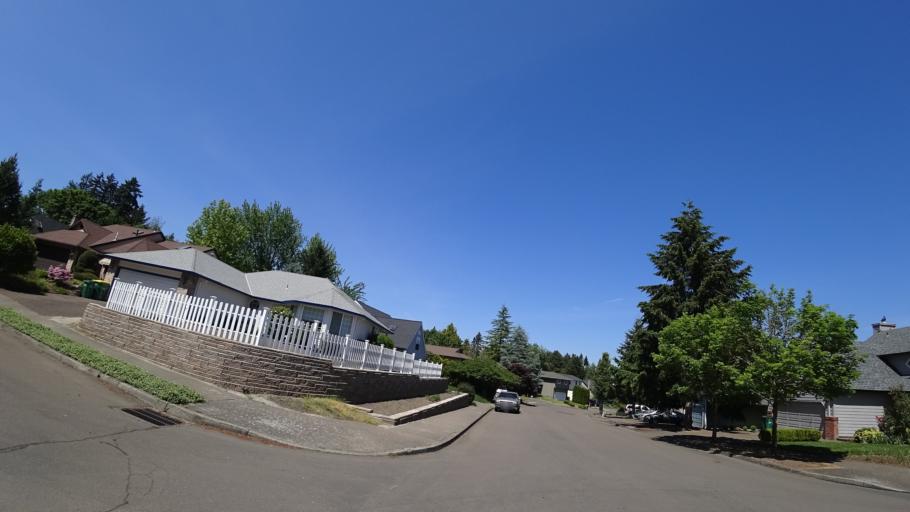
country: US
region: Oregon
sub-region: Washington County
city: King City
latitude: 45.4345
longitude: -122.8140
